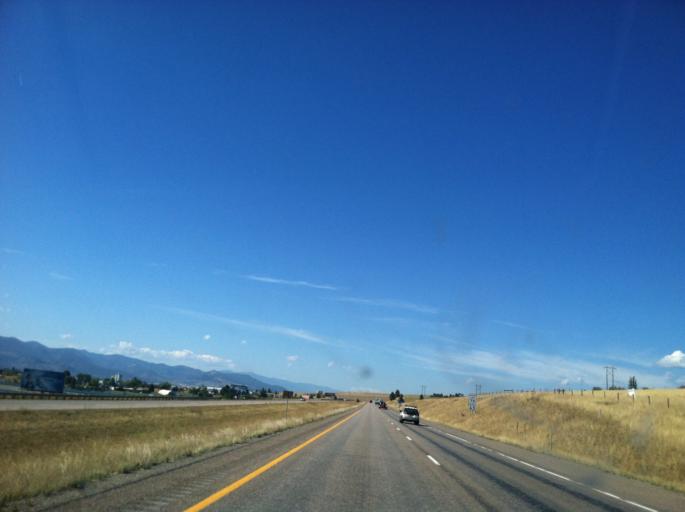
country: US
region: Montana
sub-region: Missoula County
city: Orchard Homes
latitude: 46.9299
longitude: -114.0812
